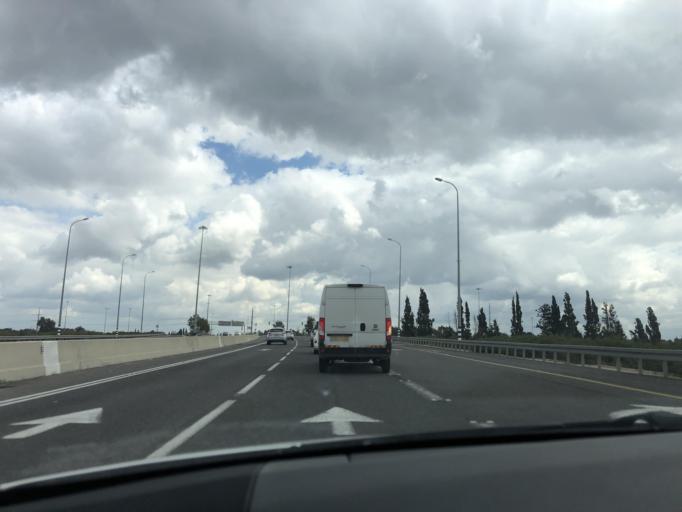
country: IL
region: Central District
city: Even Yehuda
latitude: 32.2547
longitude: 34.8857
